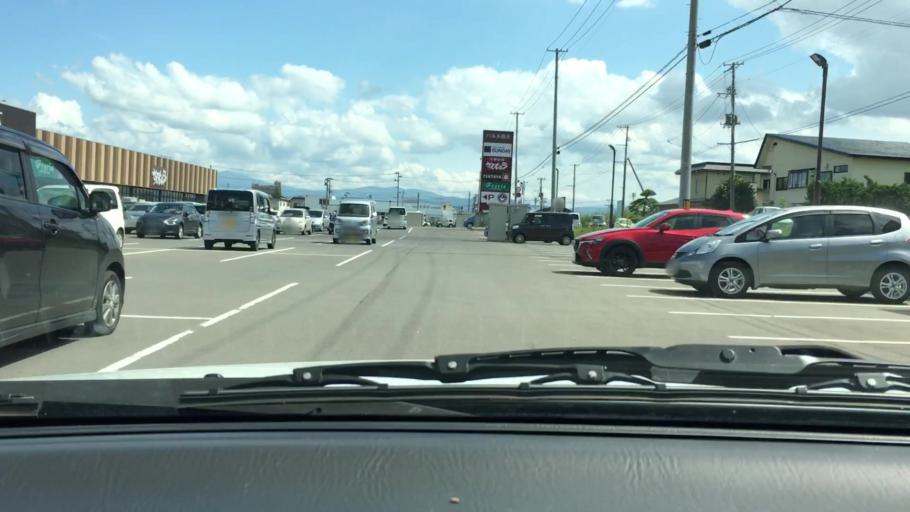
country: JP
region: Aomori
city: Hirosaki
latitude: 40.5873
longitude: 140.4586
